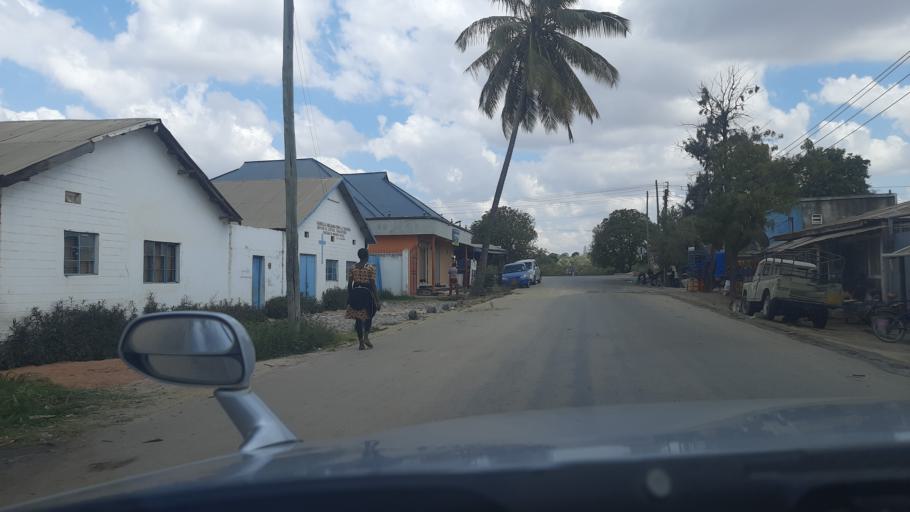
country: TZ
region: Dodoma
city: Dodoma
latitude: -6.1734
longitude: 35.7365
